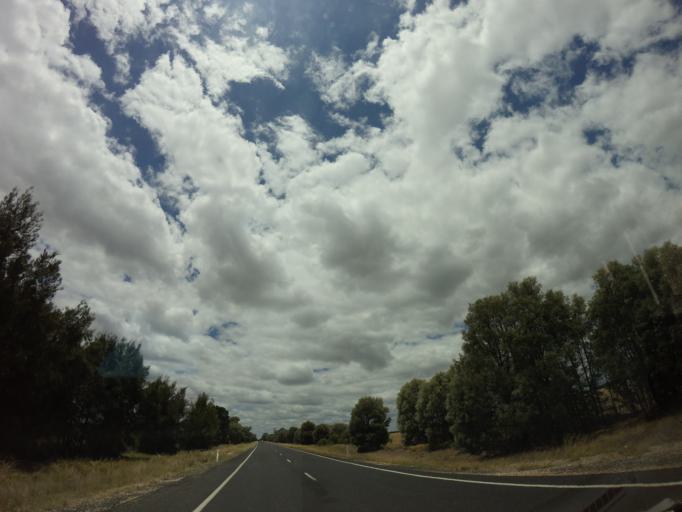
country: AU
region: Queensland
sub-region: Goondiwindi
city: Goondiwindi
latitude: -28.1712
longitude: 150.5040
